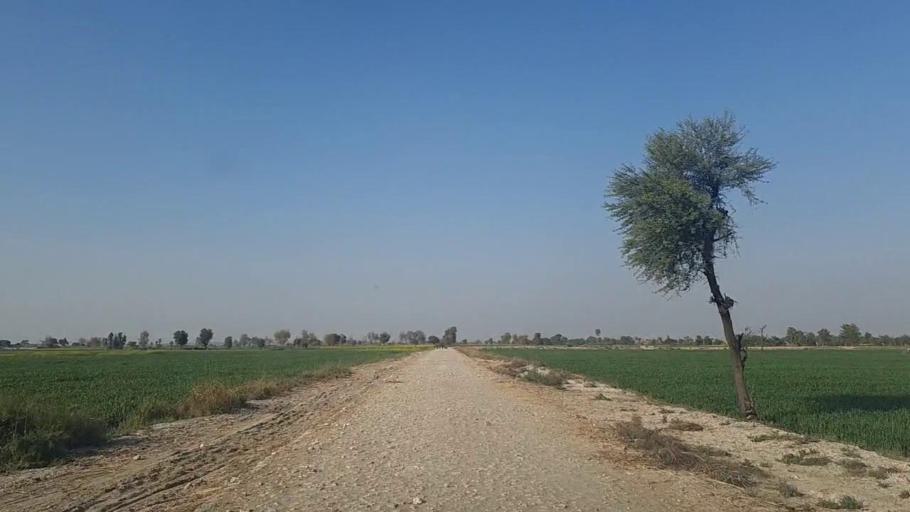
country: PK
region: Sindh
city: Jam Sahib
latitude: 26.3320
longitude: 68.7143
